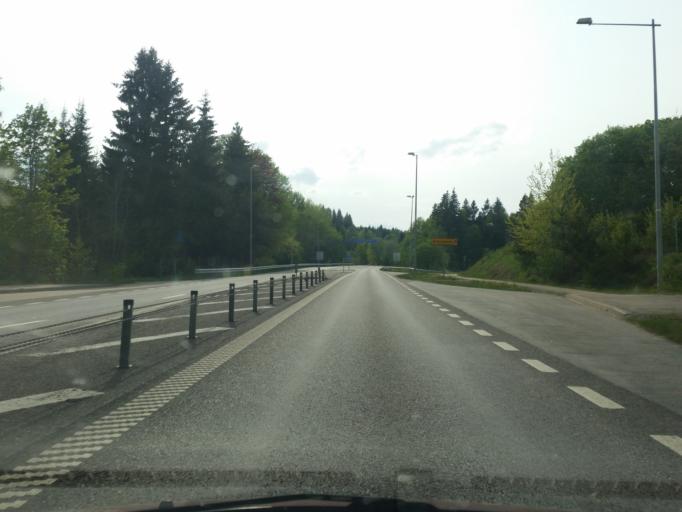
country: SE
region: Vaestra Goetaland
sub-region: Ulricehamns Kommun
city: Ulricehamn
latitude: 57.8022
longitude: 13.3461
